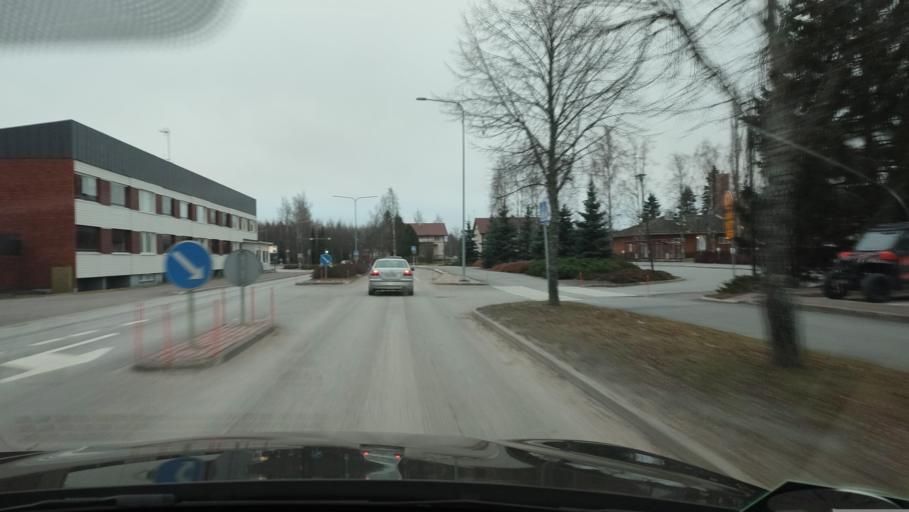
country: FI
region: Southern Ostrobothnia
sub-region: Suupohja
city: Kauhajoki
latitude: 62.4230
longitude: 22.1756
